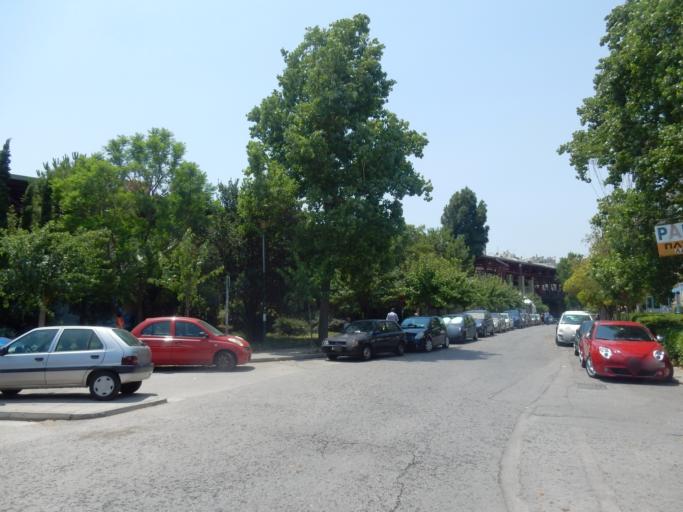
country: GR
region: Attica
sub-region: Nomarchia Athinas
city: Nea Chalkidona
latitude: 38.0246
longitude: 23.7364
